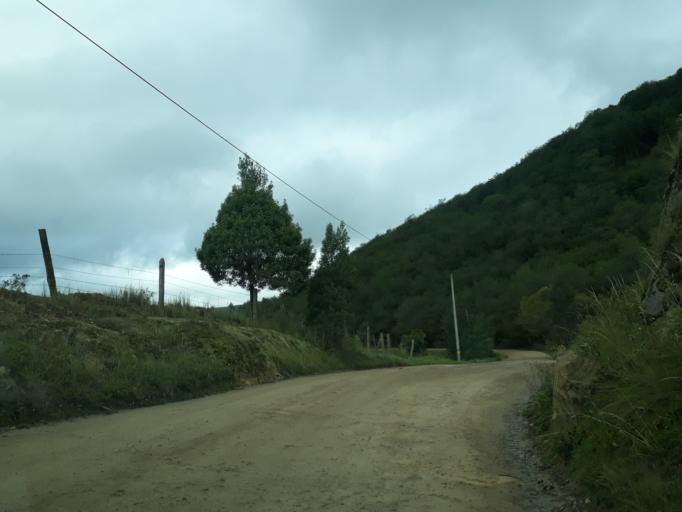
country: CO
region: Cundinamarca
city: Cucunuba
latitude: 5.2024
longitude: -73.7615
